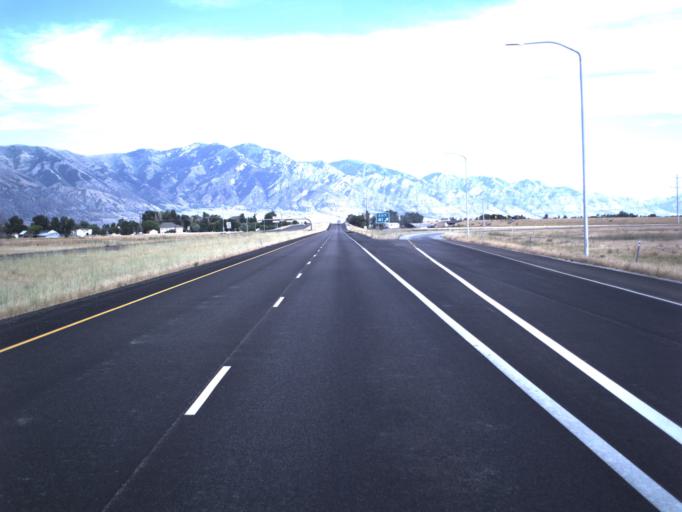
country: US
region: Utah
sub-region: Box Elder County
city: Tremonton
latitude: 41.7033
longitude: -112.1904
